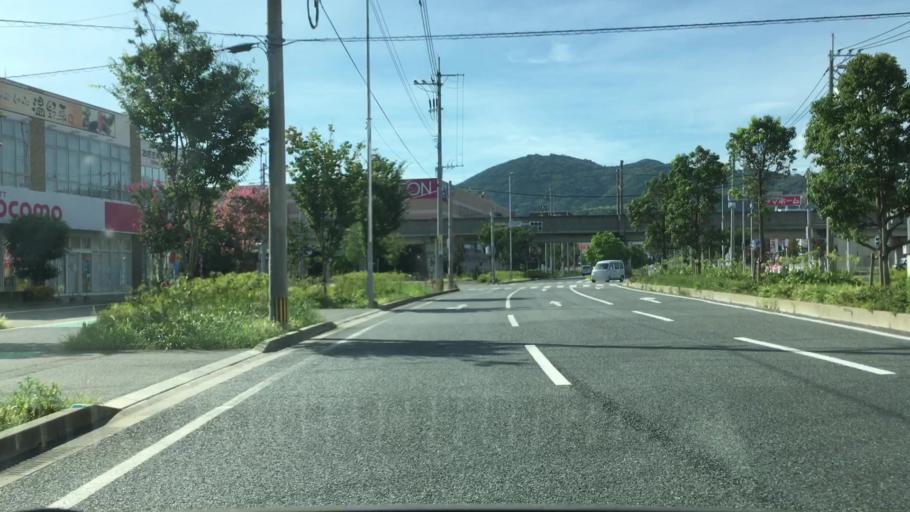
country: JP
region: Fukuoka
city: Maebaru-chuo
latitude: 33.5784
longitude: 130.2551
